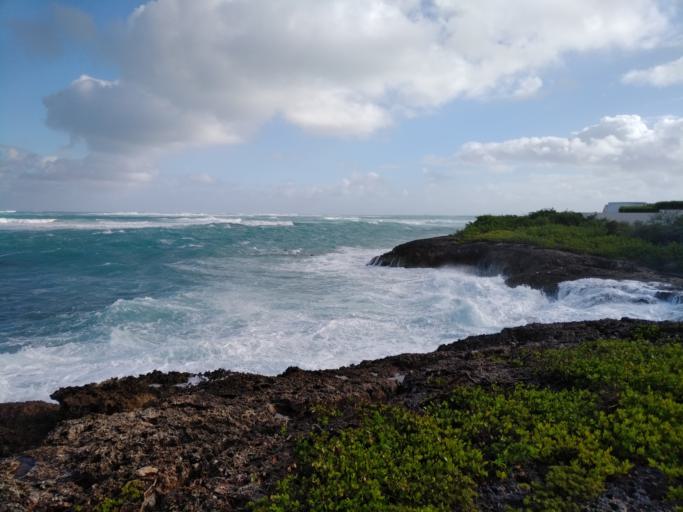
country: AI
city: Island Harbour
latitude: 18.2602
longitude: -63.0093
